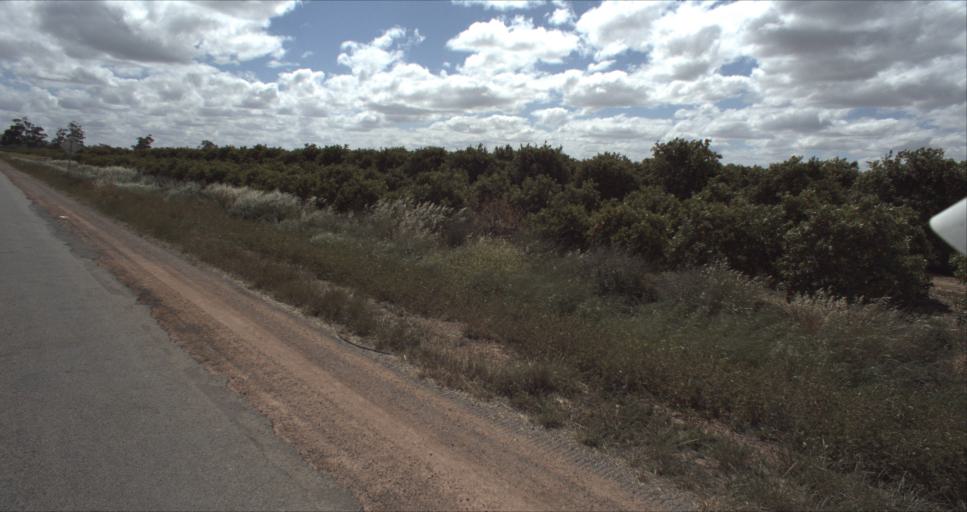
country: AU
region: New South Wales
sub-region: Leeton
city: Leeton
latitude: -34.5878
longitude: 146.3776
